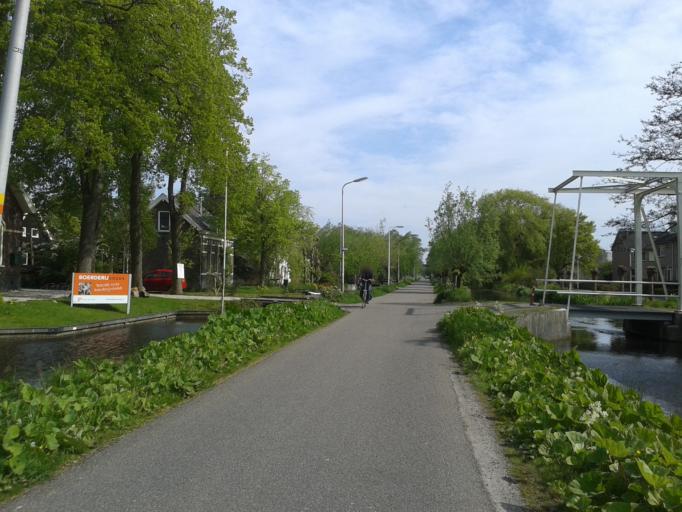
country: NL
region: South Holland
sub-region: Gemeente Gouda
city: Bloemendaal
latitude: 52.0290
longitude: 4.6999
